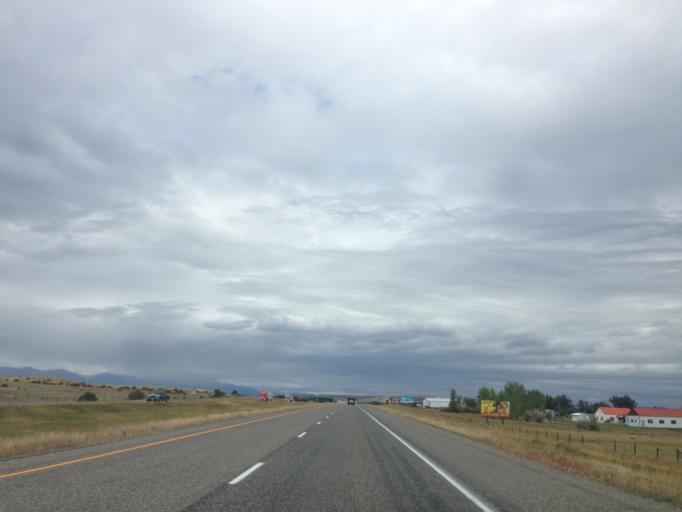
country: US
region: Montana
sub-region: Sweet Grass County
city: Big Timber
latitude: 45.7597
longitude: -109.7850
